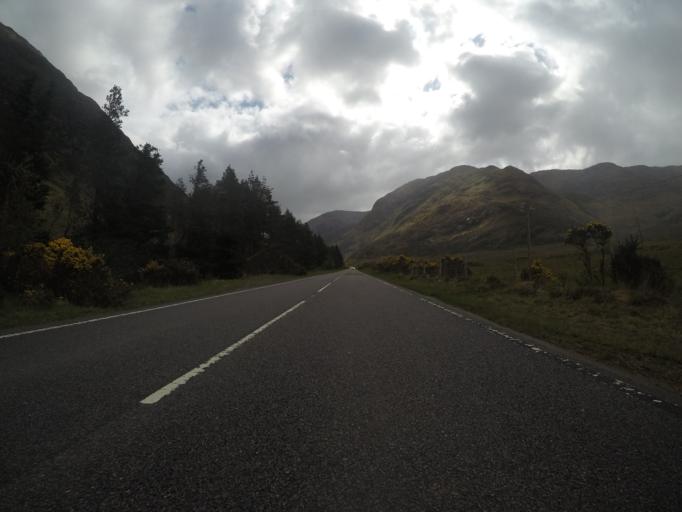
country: GB
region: Scotland
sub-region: Highland
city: Fort William
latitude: 57.1716
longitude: -5.3580
